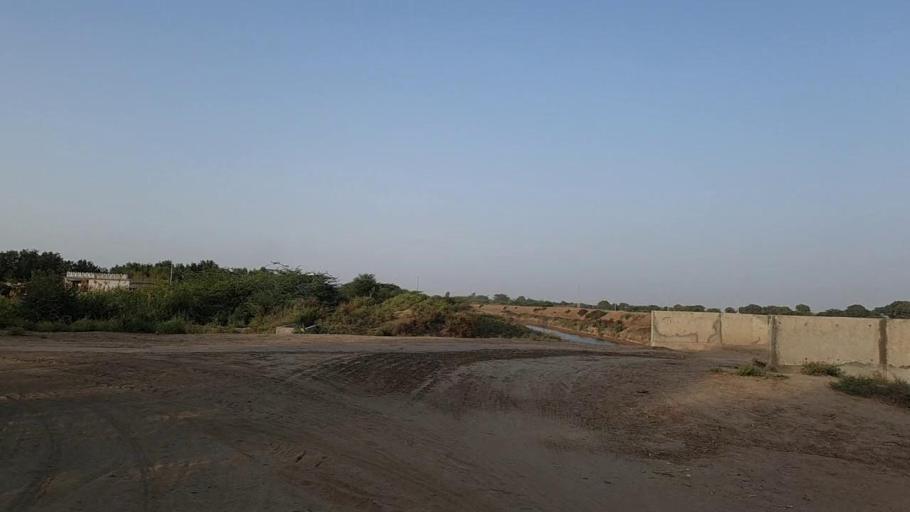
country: PK
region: Sindh
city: Jati
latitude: 24.4153
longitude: 68.1868
